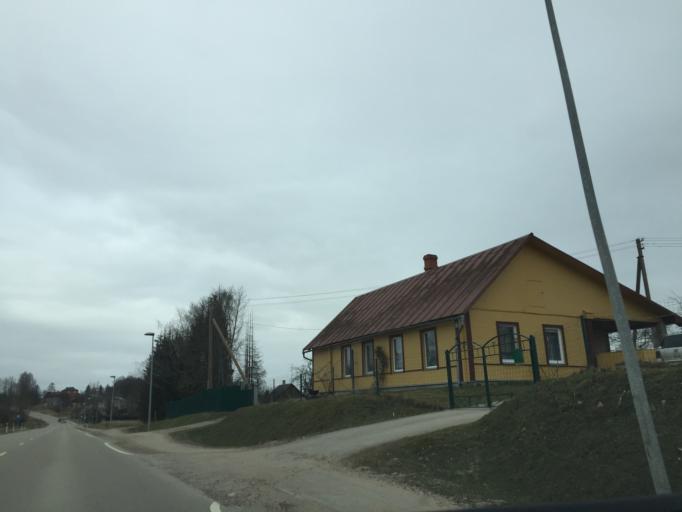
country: LV
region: Kraslavas Rajons
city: Kraslava
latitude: 55.9068
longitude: 27.1545
